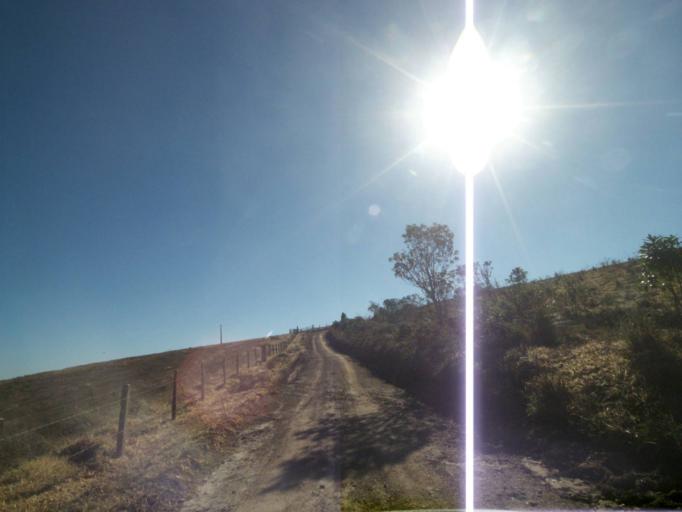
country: BR
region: Parana
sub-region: Tibagi
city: Tibagi
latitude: -24.5804
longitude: -50.4820
